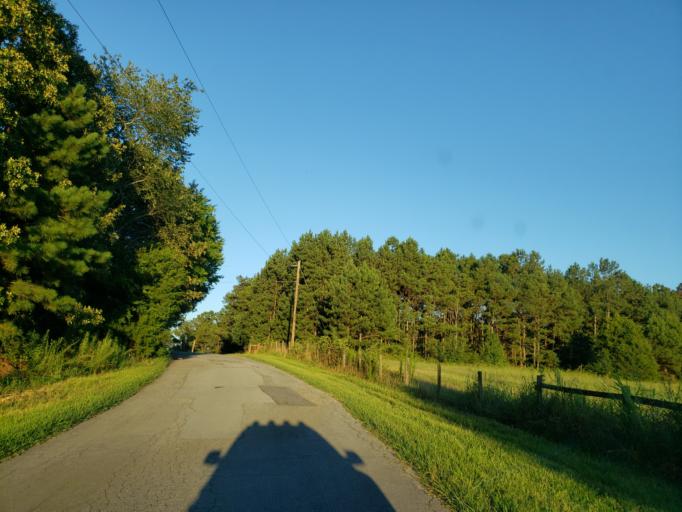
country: US
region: Georgia
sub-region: Bartow County
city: Euharlee
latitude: 34.0811
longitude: -84.9178
